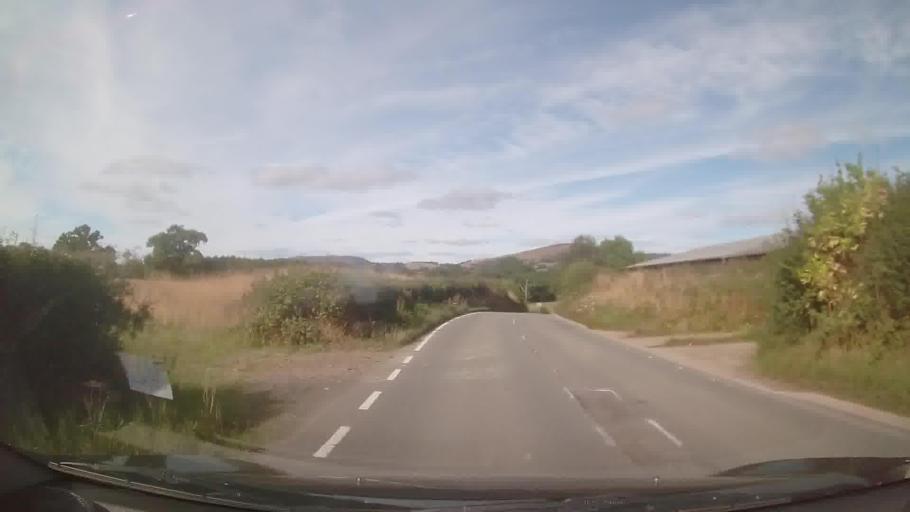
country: GB
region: England
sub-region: Shropshire
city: Lydham
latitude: 52.5088
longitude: -2.9821
